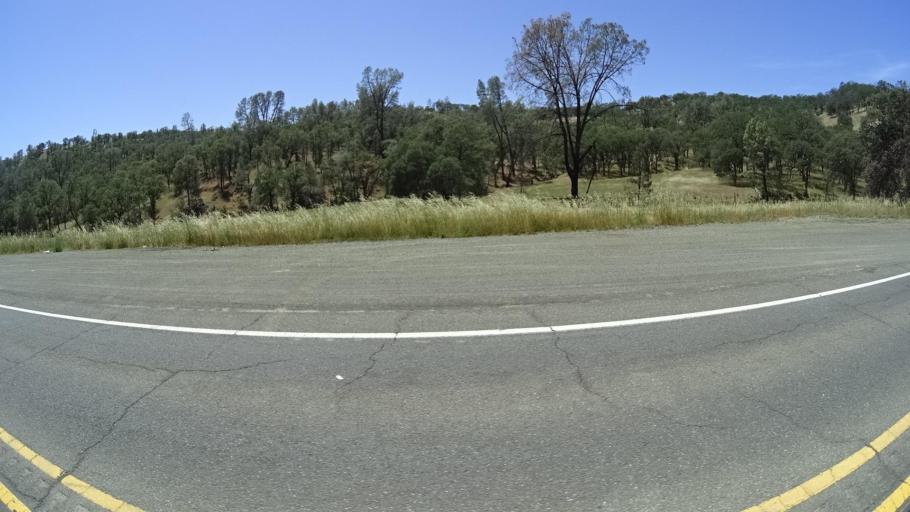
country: US
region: California
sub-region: Lake County
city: Hidden Valley Lake
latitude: 38.8286
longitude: -122.5840
